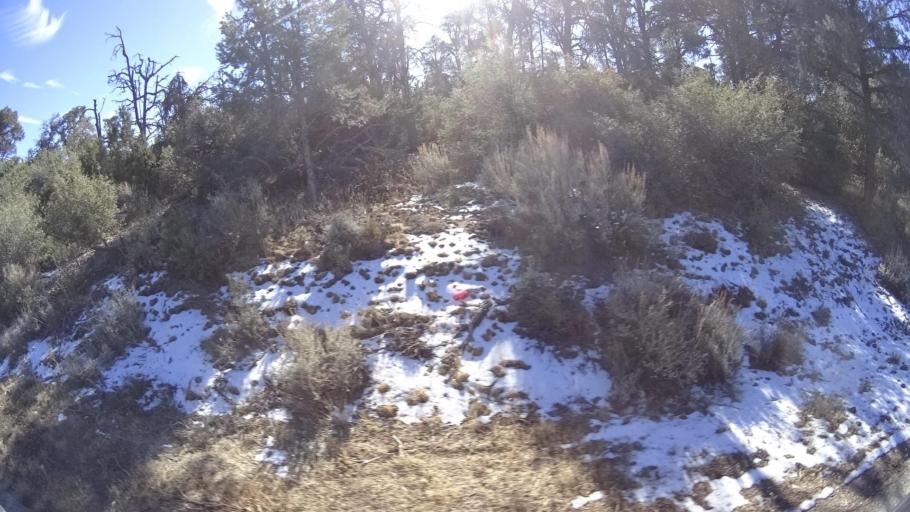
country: US
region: California
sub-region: Kern County
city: Pine Mountain Club
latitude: 34.8723
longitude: -119.2767
